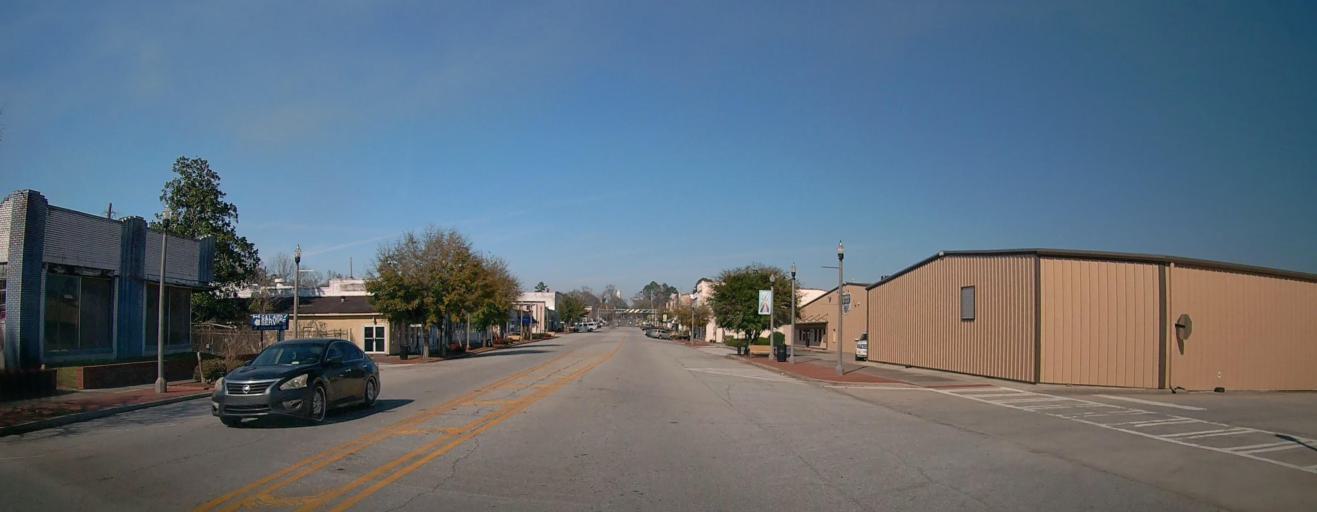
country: US
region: Georgia
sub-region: Macon County
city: Montezuma
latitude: 32.2982
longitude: -84.0312
